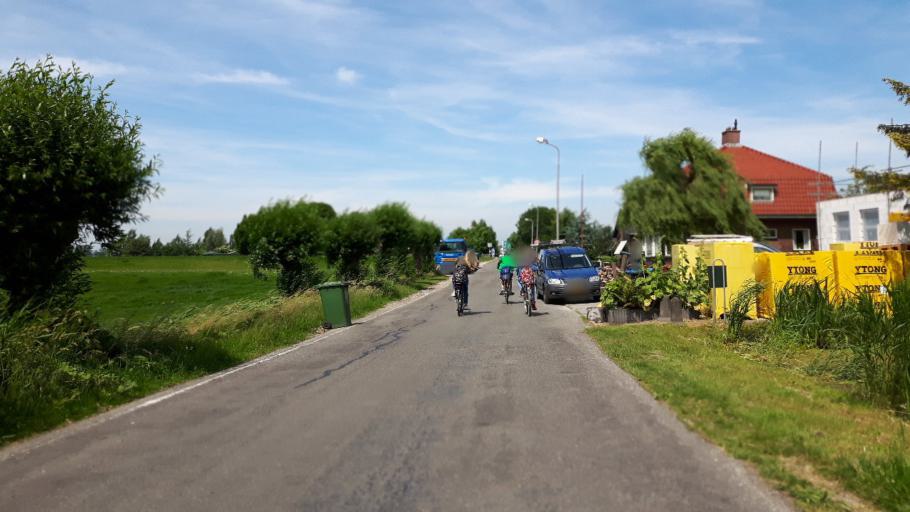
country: NL
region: South Holland
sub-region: Gemeente Nieuwkoop
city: Nieuwkoop
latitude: 52.1589
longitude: 4.7264
